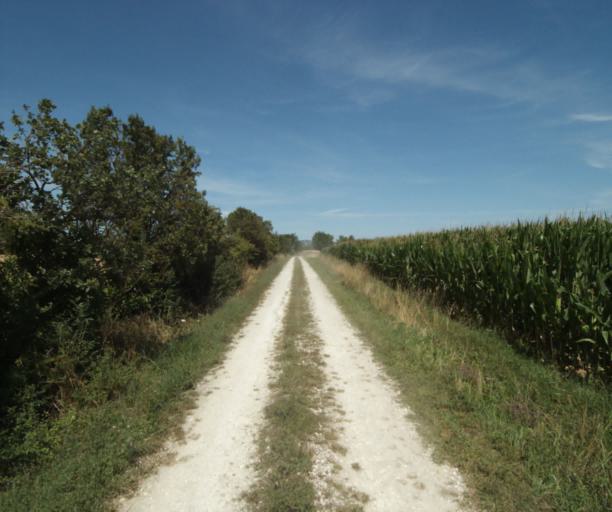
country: FR
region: Midi-Pyrenees
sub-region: Departement de la Haute-Garonne
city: Revel
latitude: 43.5018
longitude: 2.0157
